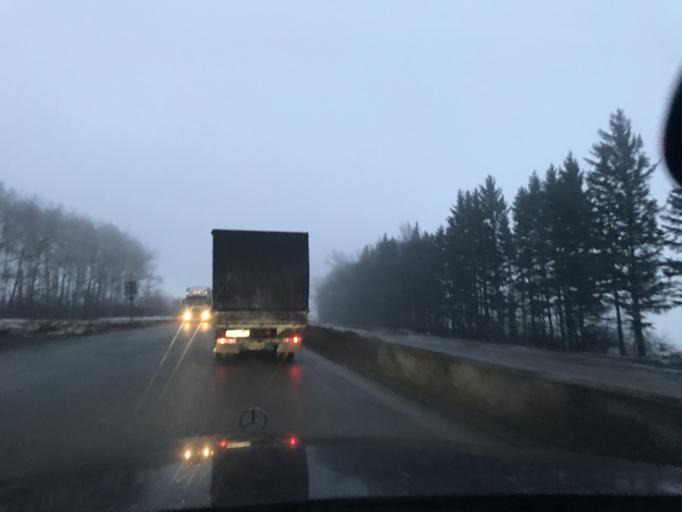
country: RU
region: Vladimir
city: Novovyazniki
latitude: 56.2158
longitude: 42.2493
